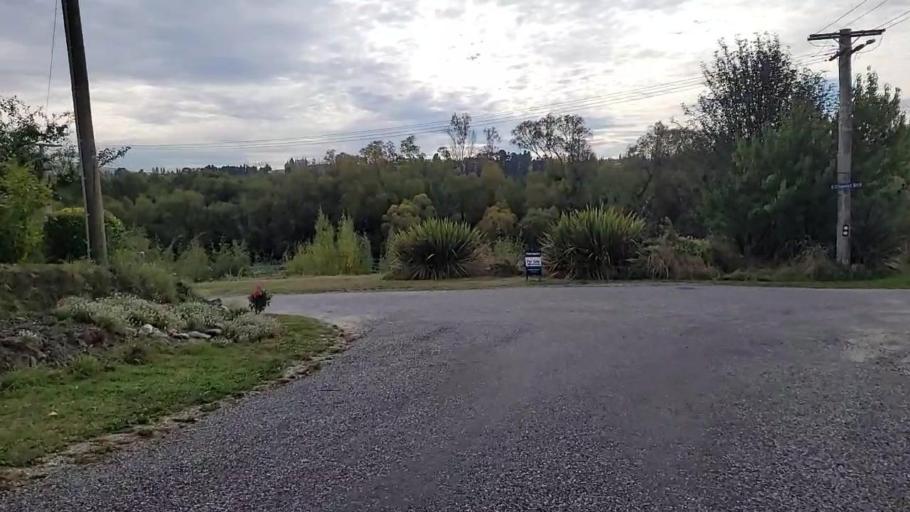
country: NZ
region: Otago
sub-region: Queenstown-Lakes District
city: Kingston
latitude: -45.5356
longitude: 169.3086
